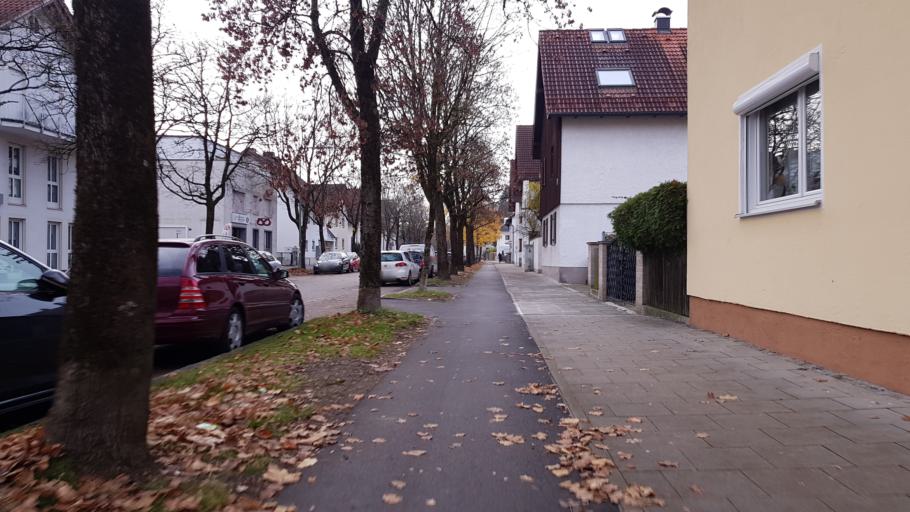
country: DE
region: Bavaria
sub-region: Upper Bavaria
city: Neubiberg
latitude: 48.0995
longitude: 11.6309
